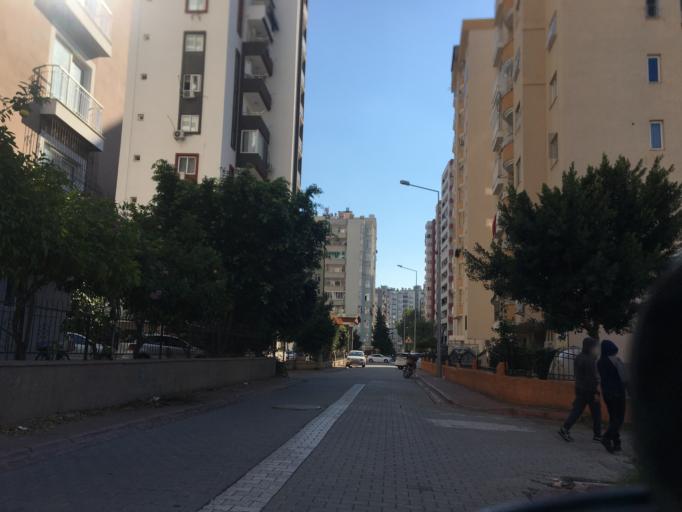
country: TR
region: Adana
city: Seyhan
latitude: 37.0252
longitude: 35.2857
